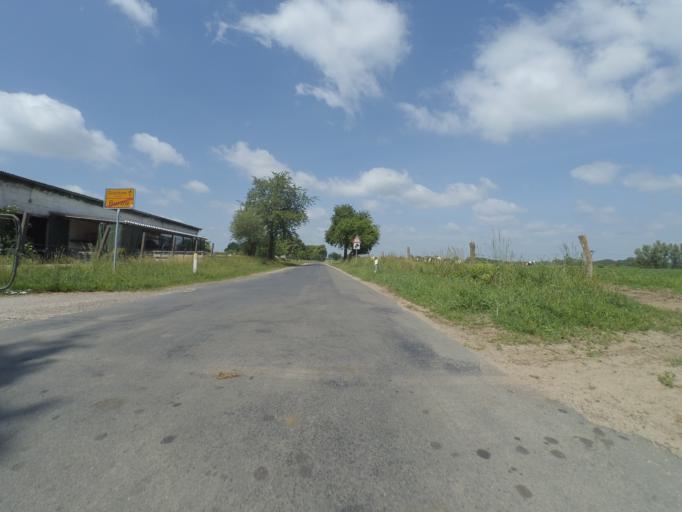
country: DE
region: Mecklenburg-Vorpommern
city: Lubz
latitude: 53.4062
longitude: 12.0140
